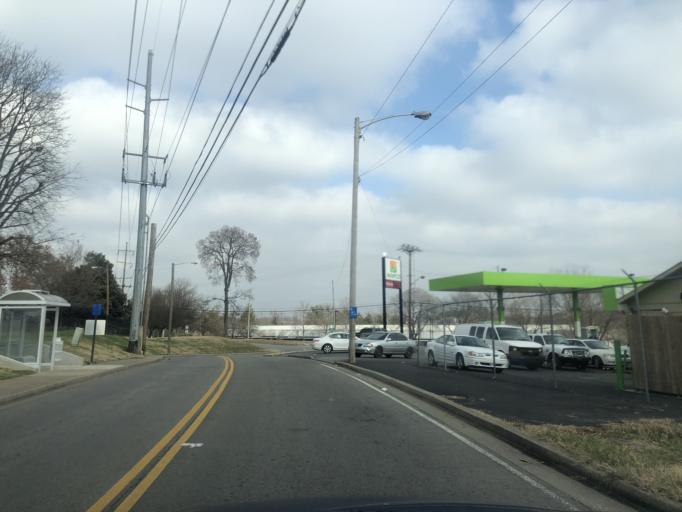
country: US
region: Tennessee
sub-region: Davidson County
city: Oak Hill
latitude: 36.0812
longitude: -86.7025
